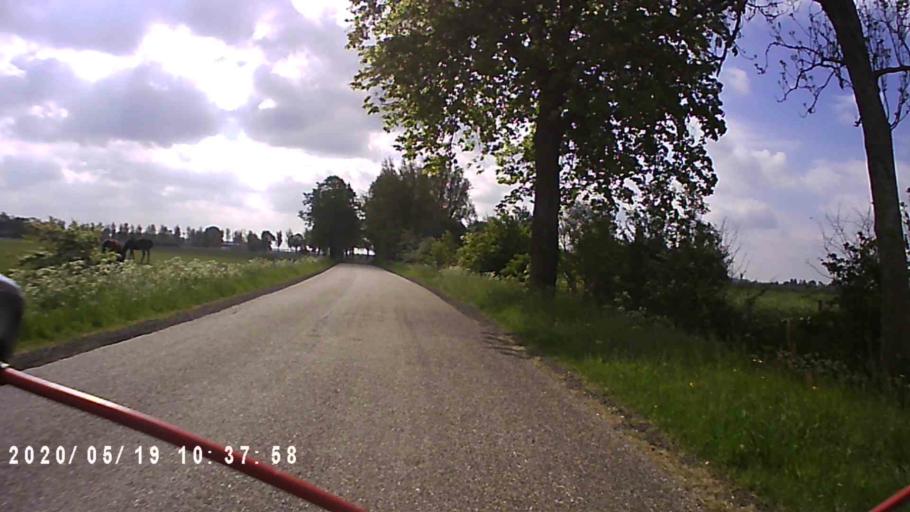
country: NL
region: Friesland
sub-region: Gemeente Kollumerland en Nieuwkruisland
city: Kollum
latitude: 53.2732
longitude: 6.1867
